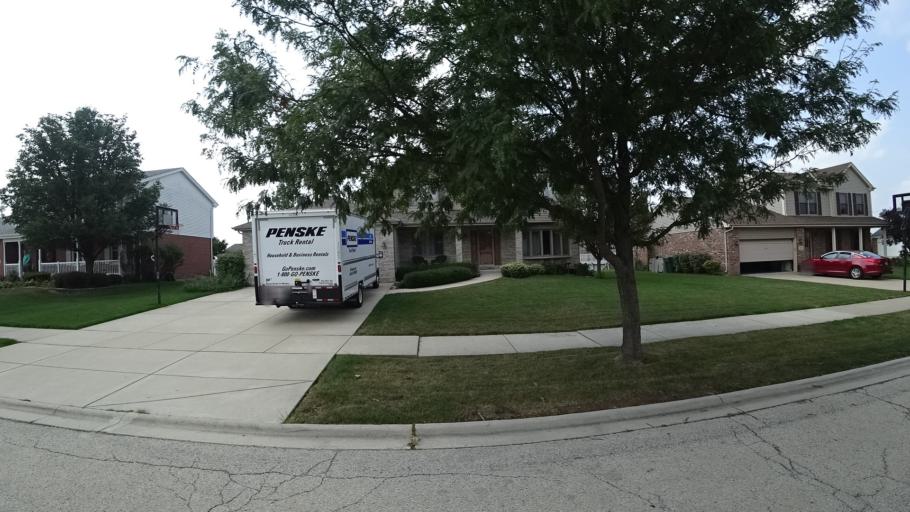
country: US
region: Illinois
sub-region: Will County
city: Goodings Grove
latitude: 41.6361
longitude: -87.8934
